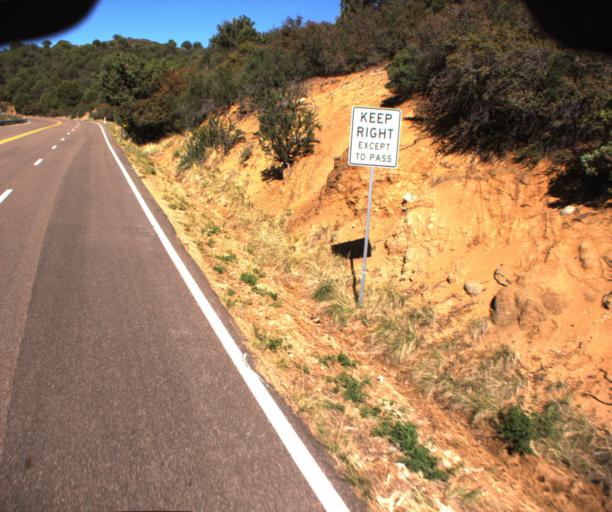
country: US
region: Arizona
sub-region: Yavapai County
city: Prescott
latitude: 34.4757
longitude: -112.5083
